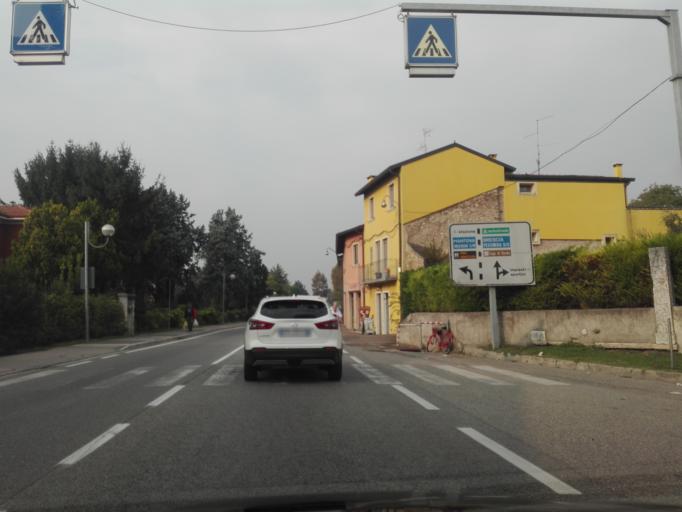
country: IT
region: Veneto
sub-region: Provincia di Verona
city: Castelnuovo del Garda
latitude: 45.4384
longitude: 10.7626
